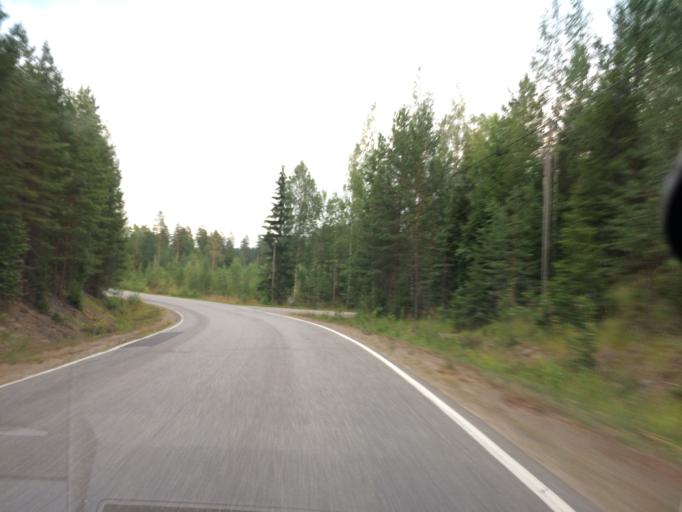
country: FI
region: Haeme
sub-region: Haemeenlinna
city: Tuulos
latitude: 61.2278
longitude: 24.7099
